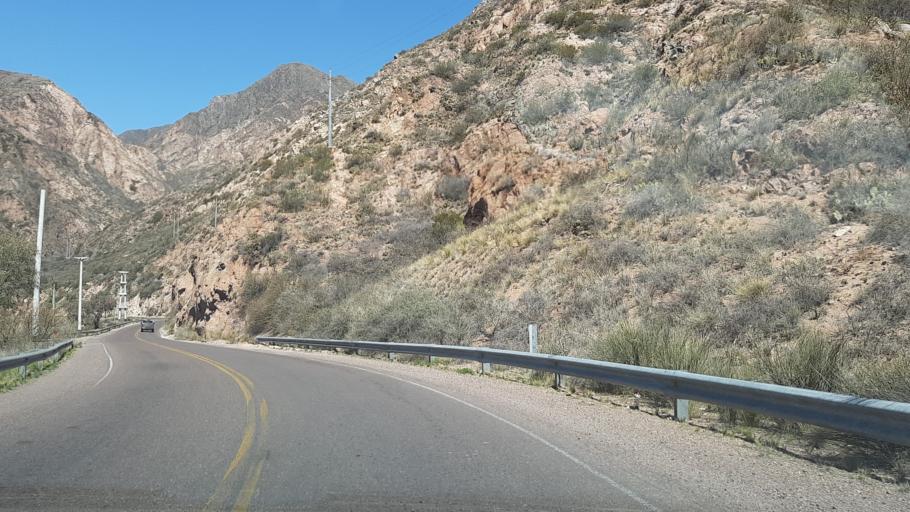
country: AR
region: Mendoza
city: Lujan de Cuyo
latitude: -33.0248
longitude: -69.1167
